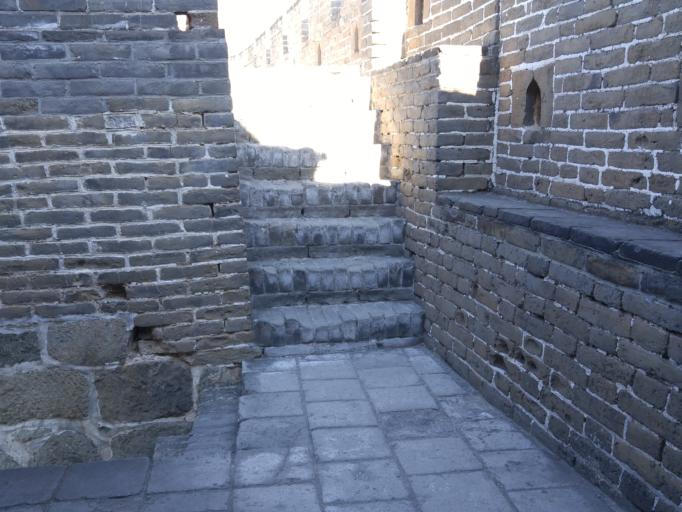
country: CN
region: Beijing
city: Bohai
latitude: 40.4385
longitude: 116.5614
